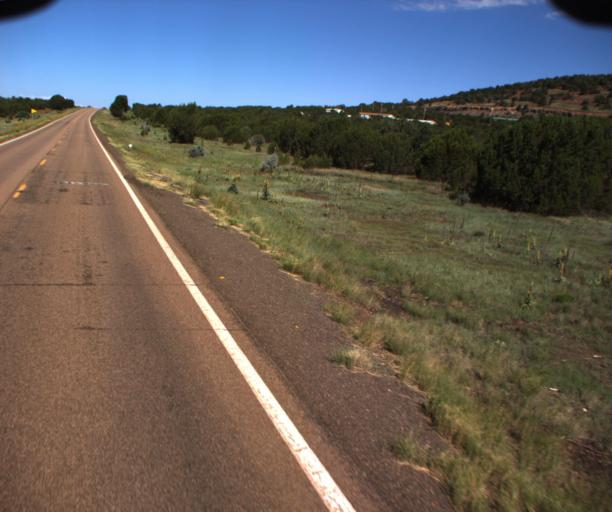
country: US
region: Arizona
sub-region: Navajo County
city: Pinetop-Lakeside
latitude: 34.2763
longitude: -109.7873
